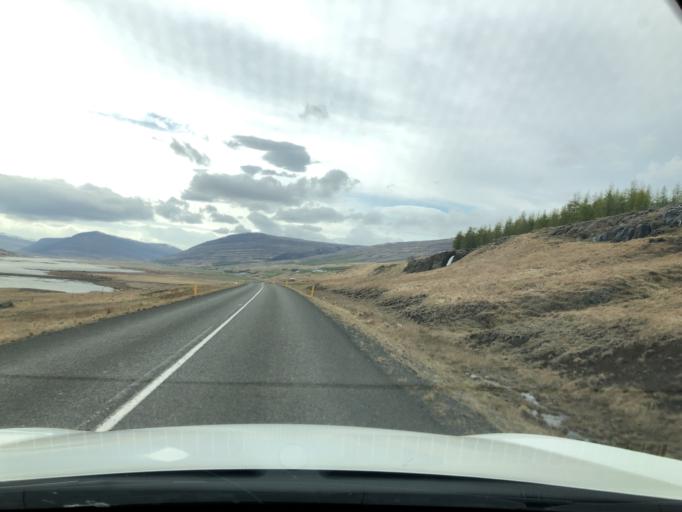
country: IS
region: East
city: Egilsstadir
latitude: 65.0828
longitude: -14.8499
